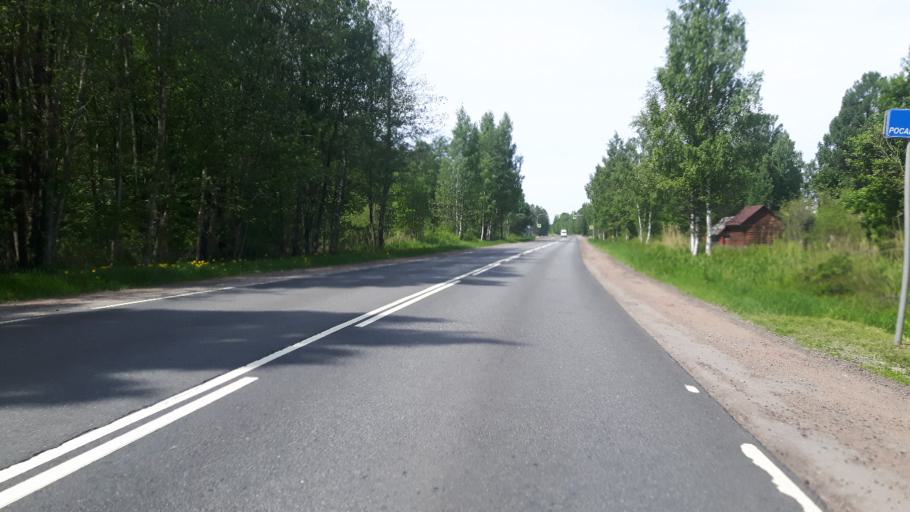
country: RU
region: Leningrad
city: Ust'-Luga
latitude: 59.6506
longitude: 28.3630
